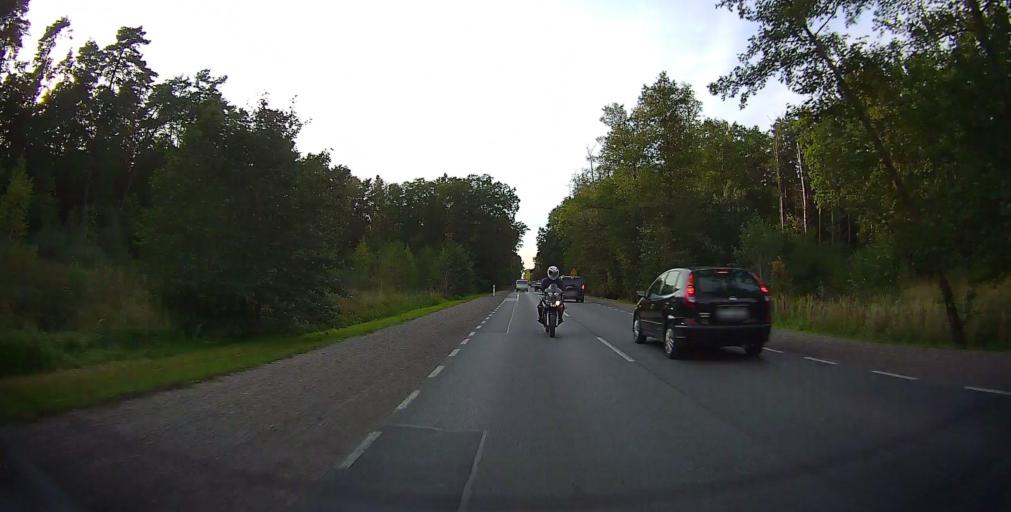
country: PL
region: Masovian Voivodeship
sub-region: Powiat piaseczynski
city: Zabieniec
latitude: 52.0496
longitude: 21.0675
